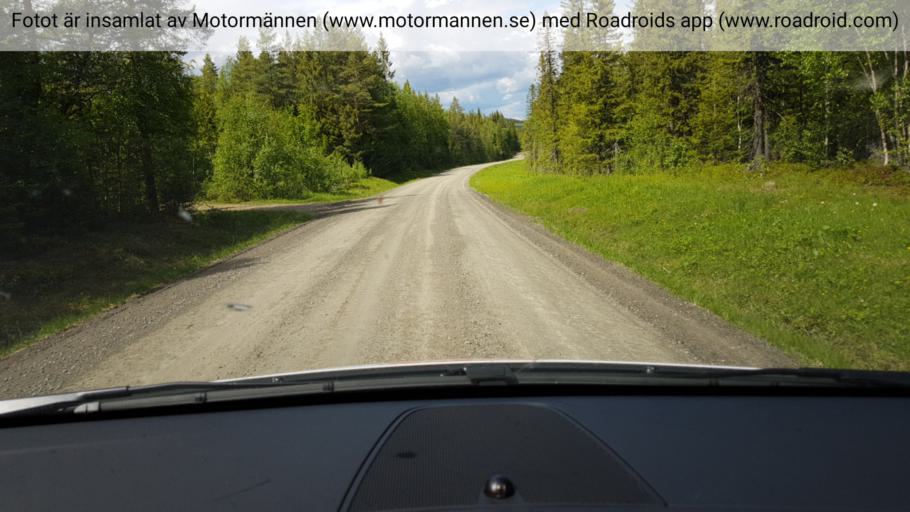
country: SE
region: Jaemtland
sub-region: Bergs Kommun
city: Hoverberg
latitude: 63.0112
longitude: 14.1118
